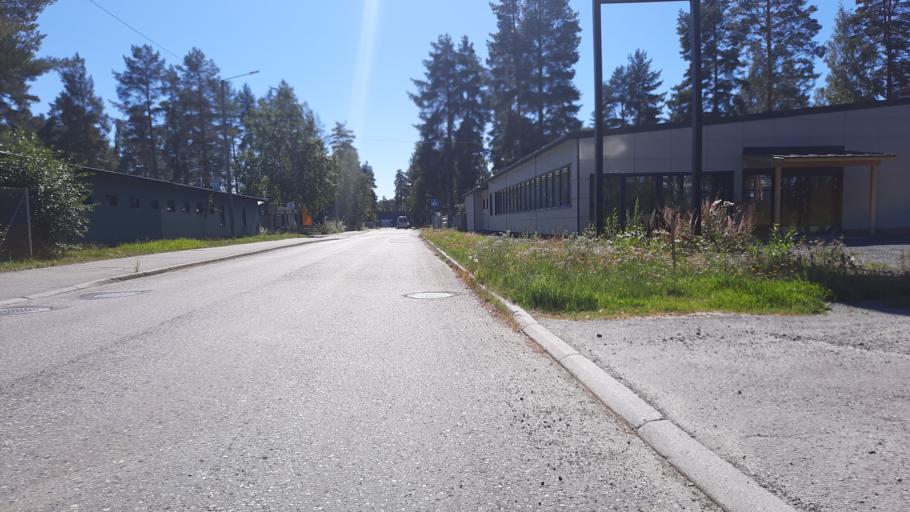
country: FI
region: North Karelia
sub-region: Joensuu
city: Joensuu
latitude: 62.6204
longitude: 29.7430
